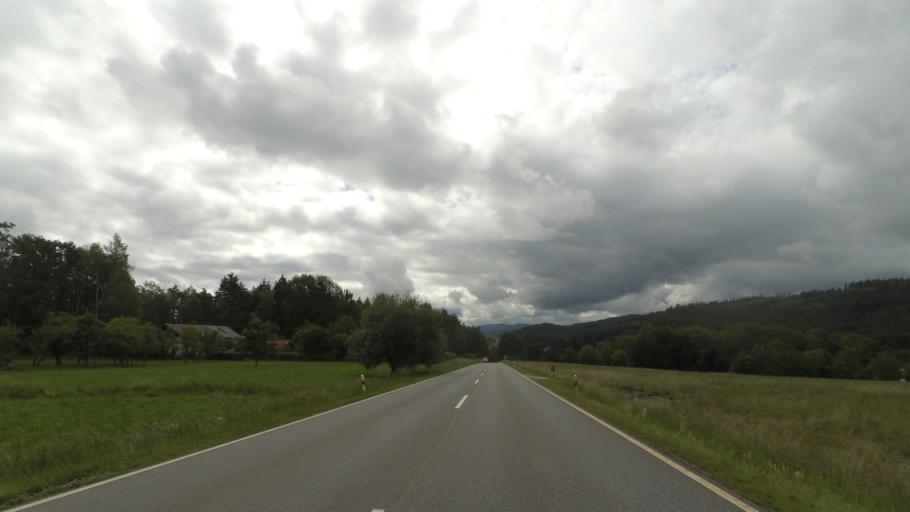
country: DE
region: Bavaria
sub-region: Lower Bavaria
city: Prackenbach
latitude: 49.0853
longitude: 12.8545
